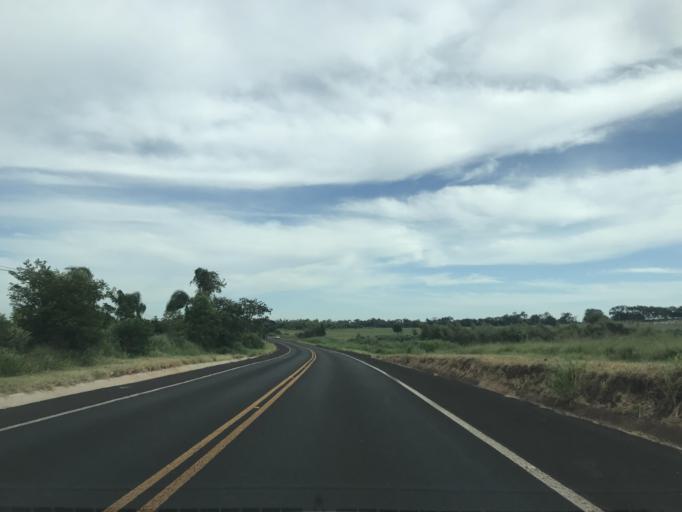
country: BR
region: Parana
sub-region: Paranavai
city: Paranavai
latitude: -23.0289
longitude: -52.4836
